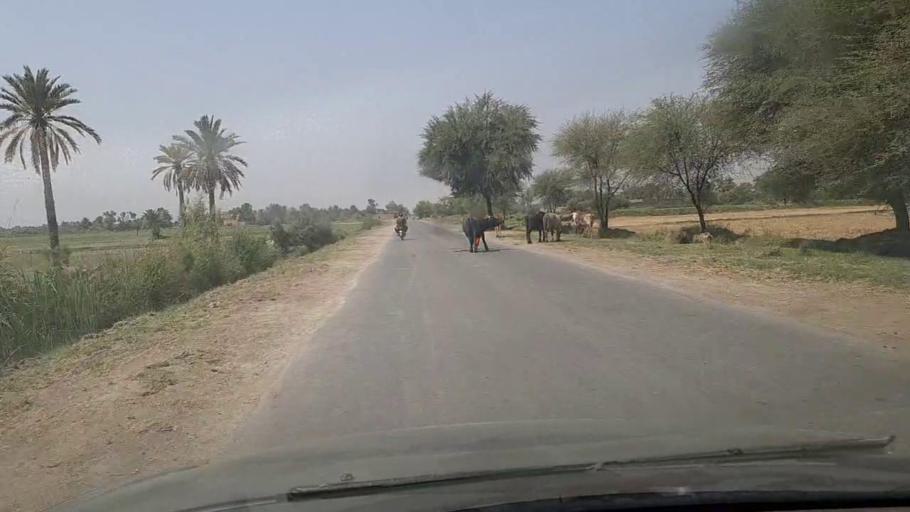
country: PK
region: Sindh
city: Khanpur
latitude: 27.8883
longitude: 69.4790
